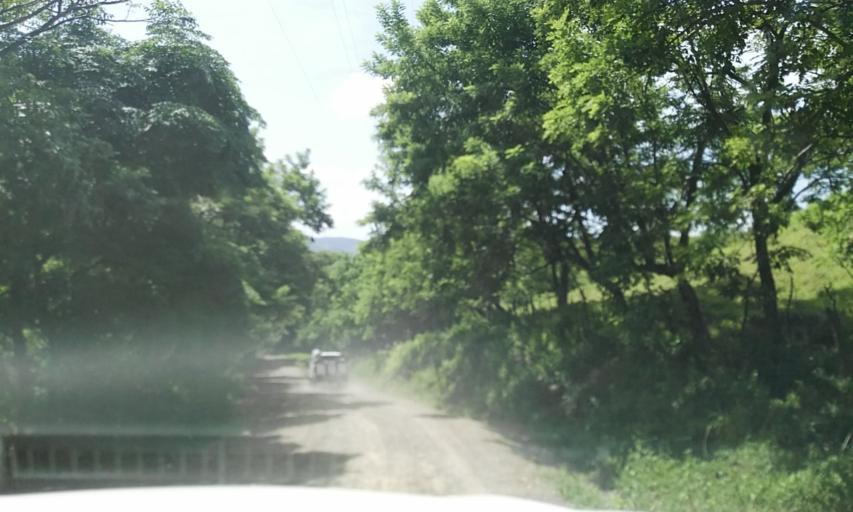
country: NI
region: Matagalpa
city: Terrabona
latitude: 12.6978
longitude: -85.9335
